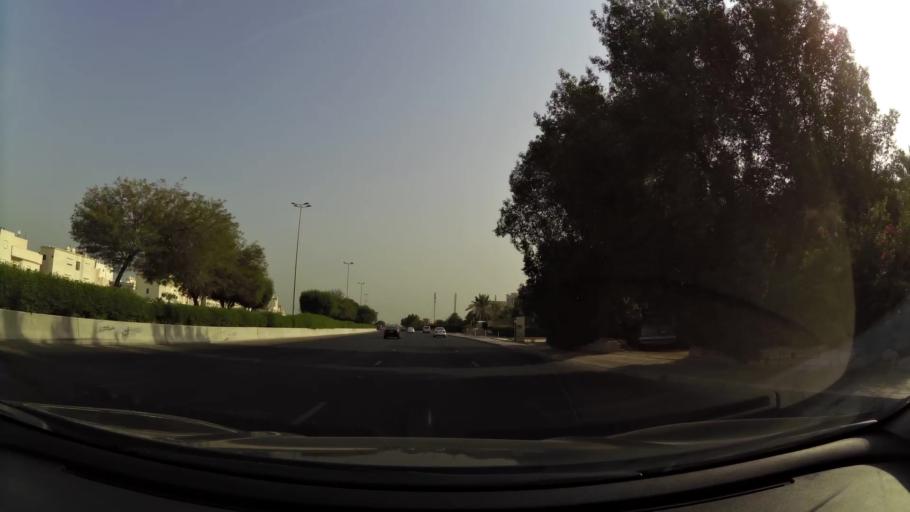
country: KW
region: Mubarak al Kabir
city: Sabah as Salim
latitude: 29.2326
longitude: 48.0732
